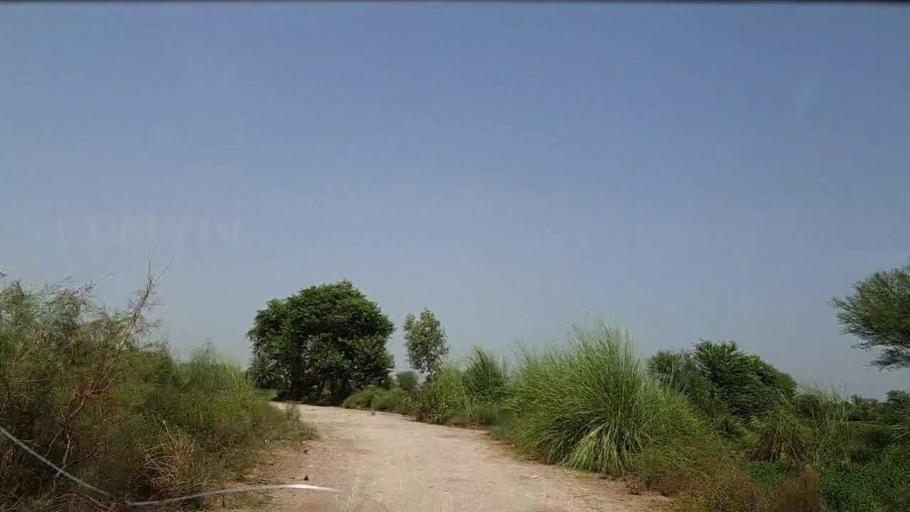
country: PK
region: Sindh
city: Tharu Shah
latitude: 26.9466
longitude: 68.0444
